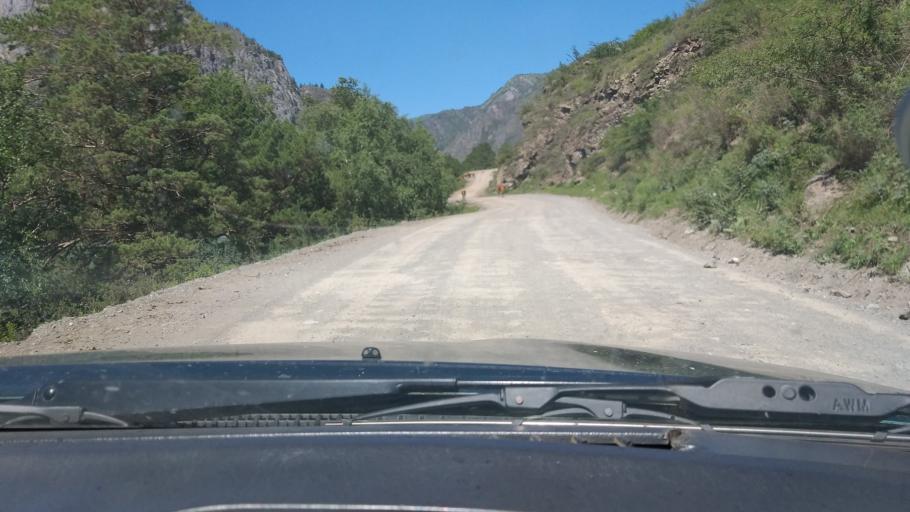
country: RU
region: Altay
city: Chemal
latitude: 51.2049
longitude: 86.0854
